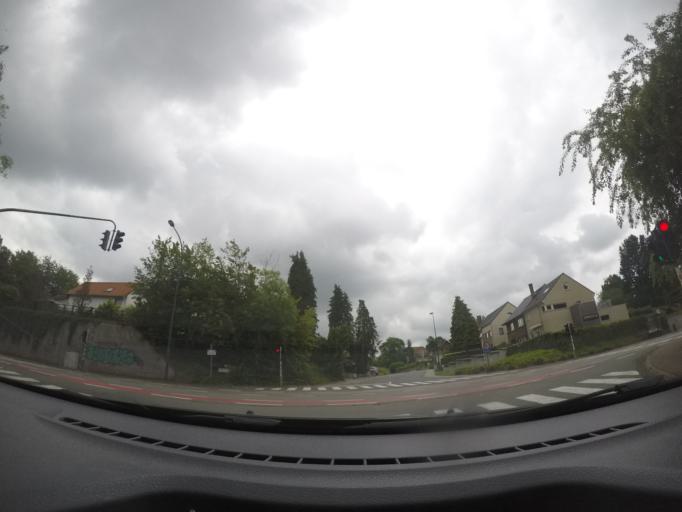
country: BE
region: Flanders
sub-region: Provincie Vlaams-Brabant
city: Sint-Genesius-Rode
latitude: 50.7457
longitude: 4.3553
